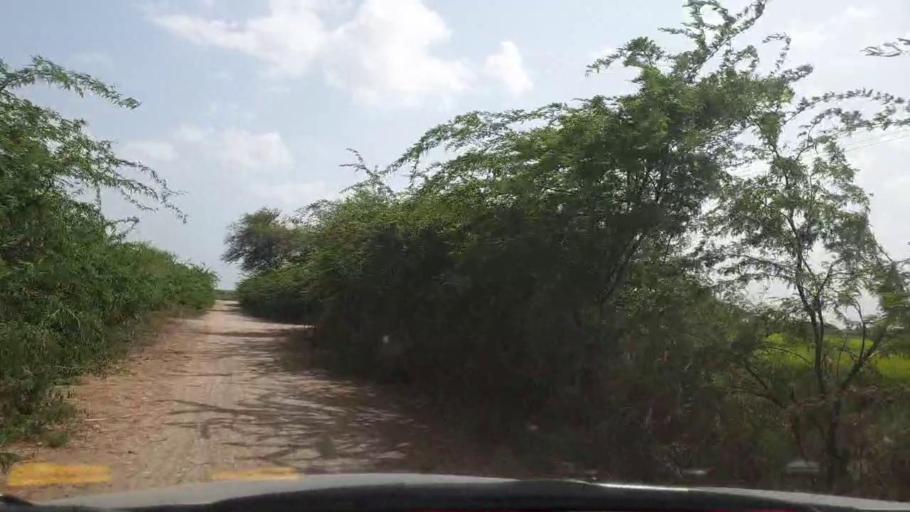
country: PK
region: Sindh
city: Talhar
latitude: 24.8555
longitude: 68.8986
